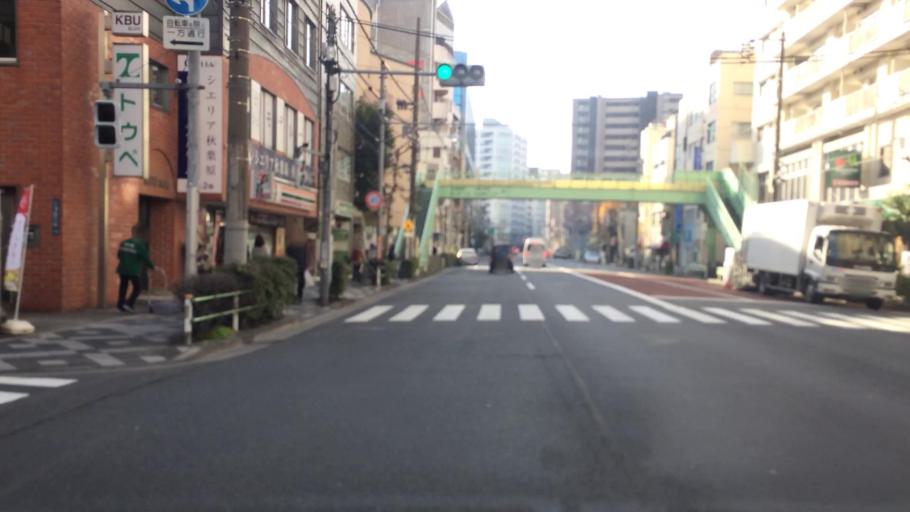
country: JP
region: Tokyo
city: Tokyo
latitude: 35.7142
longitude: 139.7830
